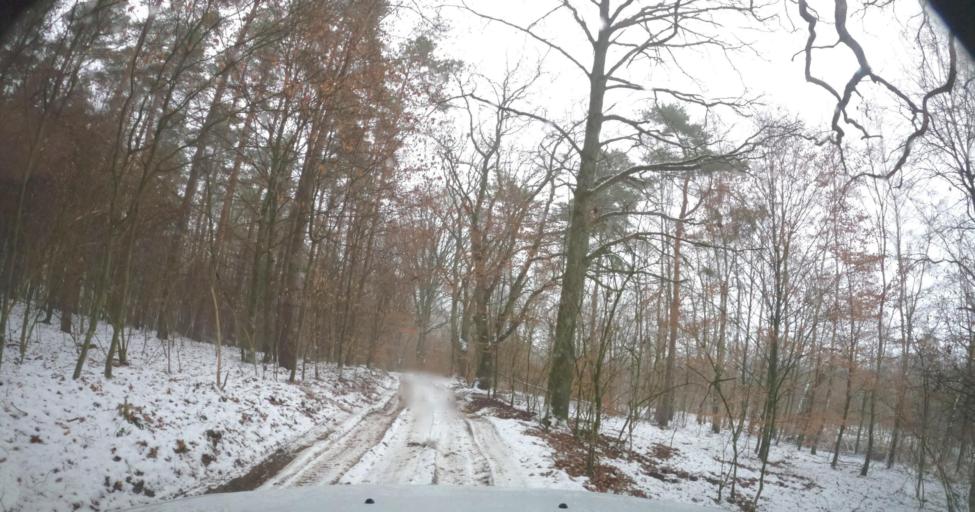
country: PL
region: West Pomeranian Voivodeship
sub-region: Powiat kamienski
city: Golczewo
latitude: 53.8694
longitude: 15.0480
